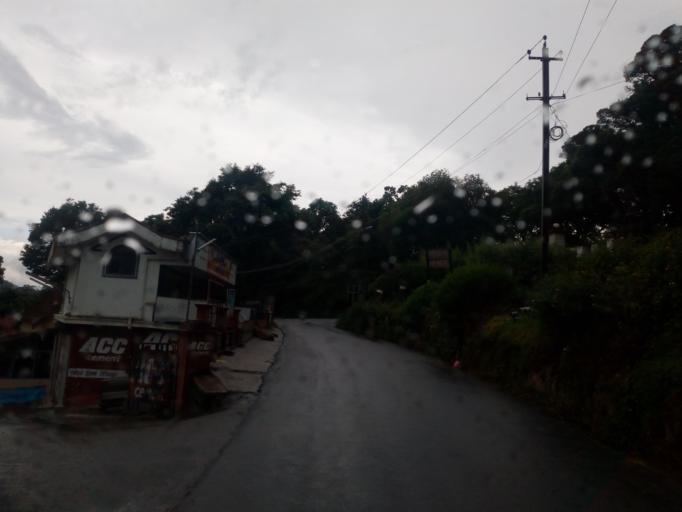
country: IN
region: Tamil Nadu
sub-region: Nilgiri
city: Wellington
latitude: 11.3465
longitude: 76.8018
